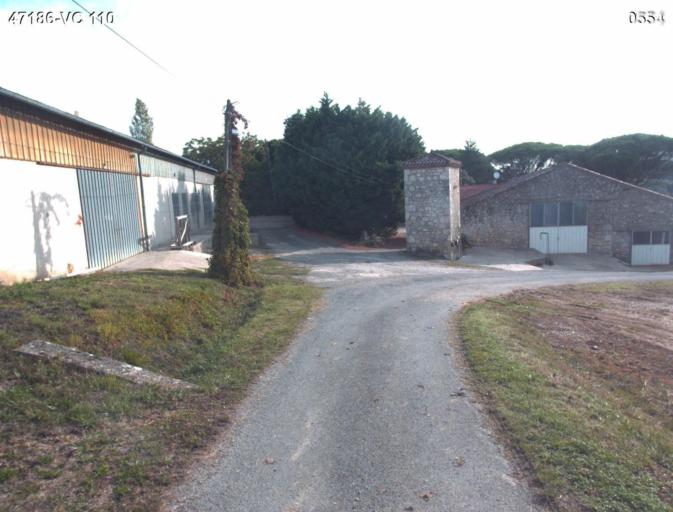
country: FR
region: Aquitaine
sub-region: Departement du Lot-et-Garonne
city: Sainte-Colombe-en-Bruilhois
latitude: 44.1886
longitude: 0.4381
